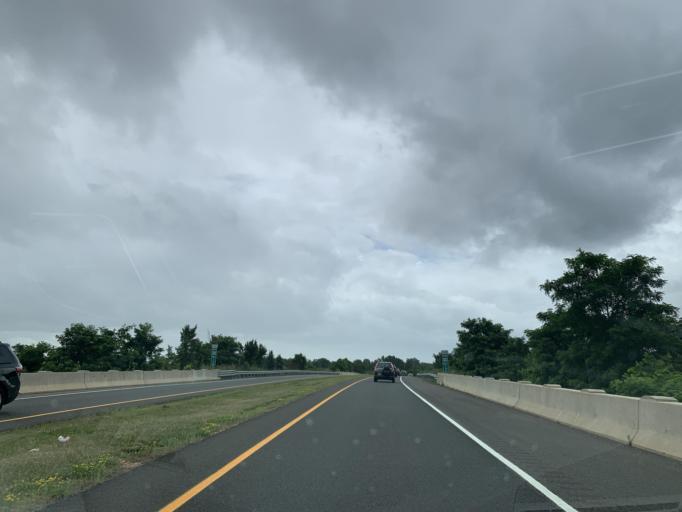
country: US
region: New Jersey
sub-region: Somerset County
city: Bloomingdale
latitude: 40.4876
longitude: -74.6394
